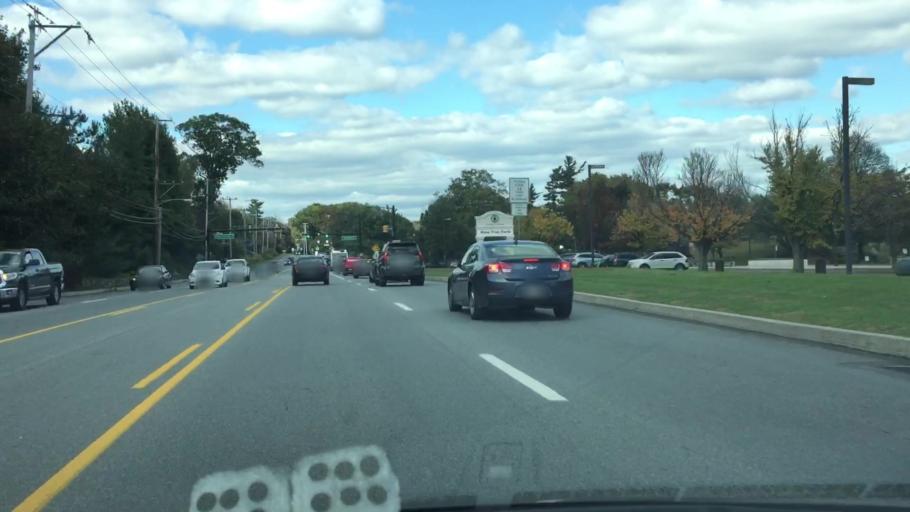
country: US
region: Pennsylvania
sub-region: Delaware County
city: Media
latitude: 39.9391
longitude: -75.3942
